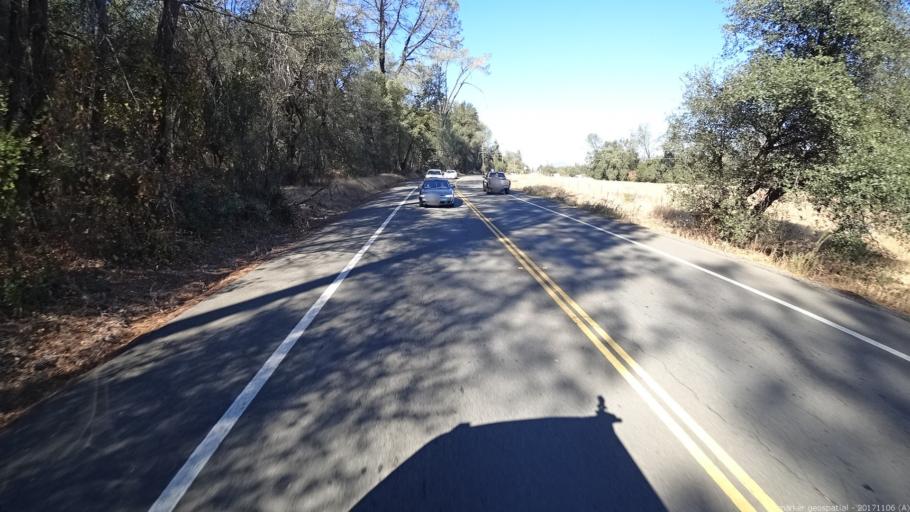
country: US
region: California
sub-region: Shasta County
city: Palo Cedro
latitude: 40.5890
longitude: -122.3073
